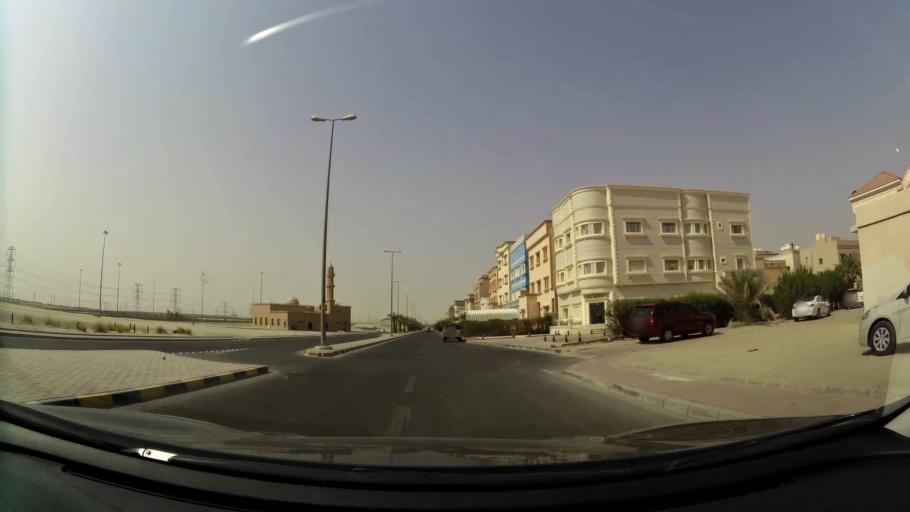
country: KW
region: Muhafazat al Jahra'
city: Al Jahra'
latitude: 29.2997
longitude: 47.7190
